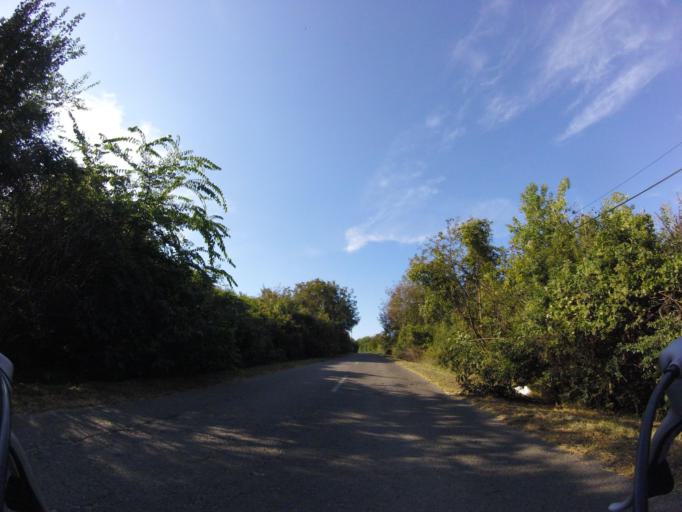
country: HU
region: Pest
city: Uri
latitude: 47.3927
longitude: 19.4978
